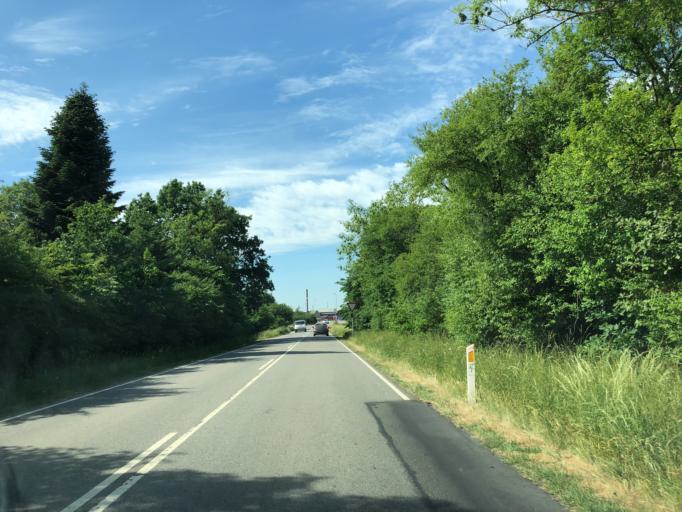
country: DK
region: Central Jutland
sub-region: Ikast-Brande Kommune
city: Brande
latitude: 55.9249
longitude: 9.1596
